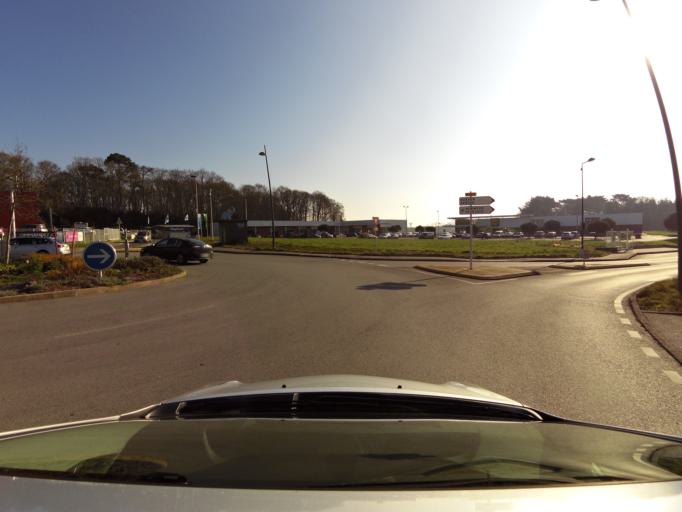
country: FR
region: Brittany
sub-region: Departement du Morbihan
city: Gestel
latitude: 47.7994
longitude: -3.4772
